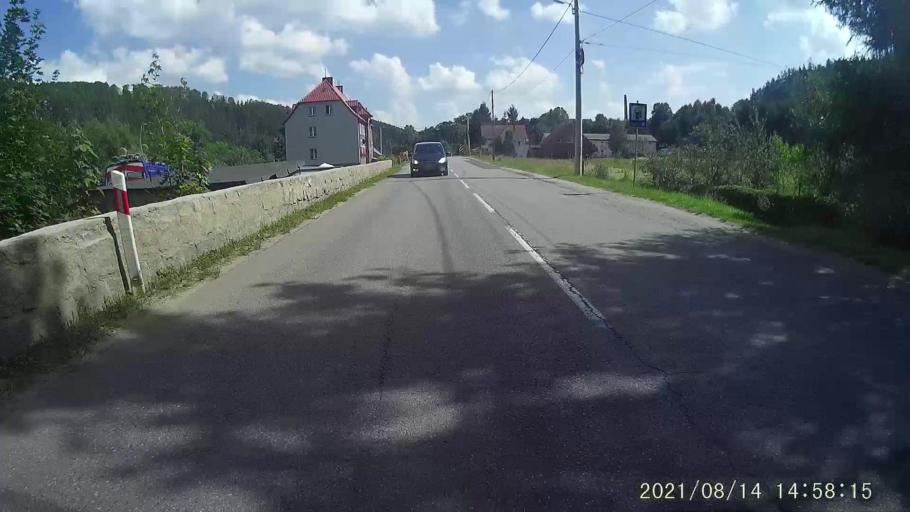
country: PL
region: Lower Silesian Voivodeship
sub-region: Powiat walbrzyski
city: Gluszyca
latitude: 50.7026
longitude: 16.3636
